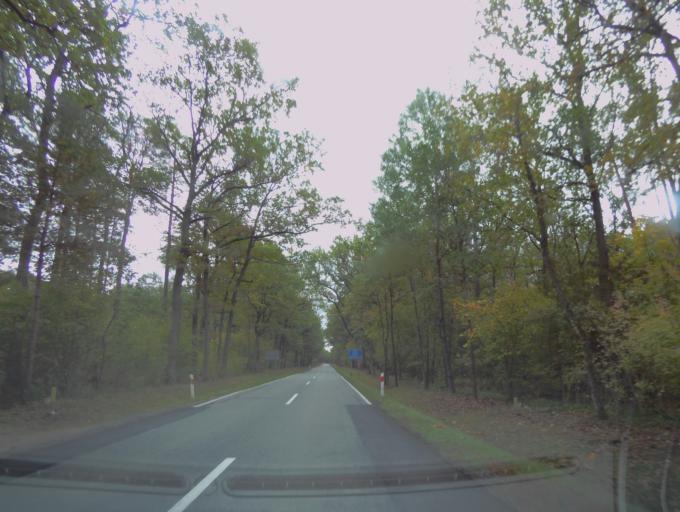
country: PL
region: Subcarpathian Voivodeship
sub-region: Powiat nizanski
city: Krzeszow
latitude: 50.3891
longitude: 22.3047
